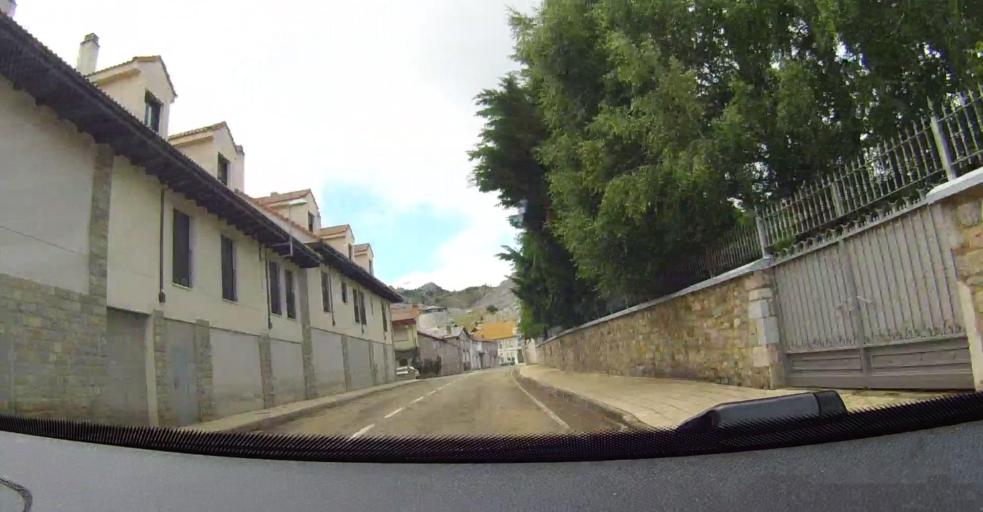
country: ES
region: Castille and Leon
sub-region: Provincia de Leon
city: Puebla de Lillo
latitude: 43.0064
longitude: -5.2730
